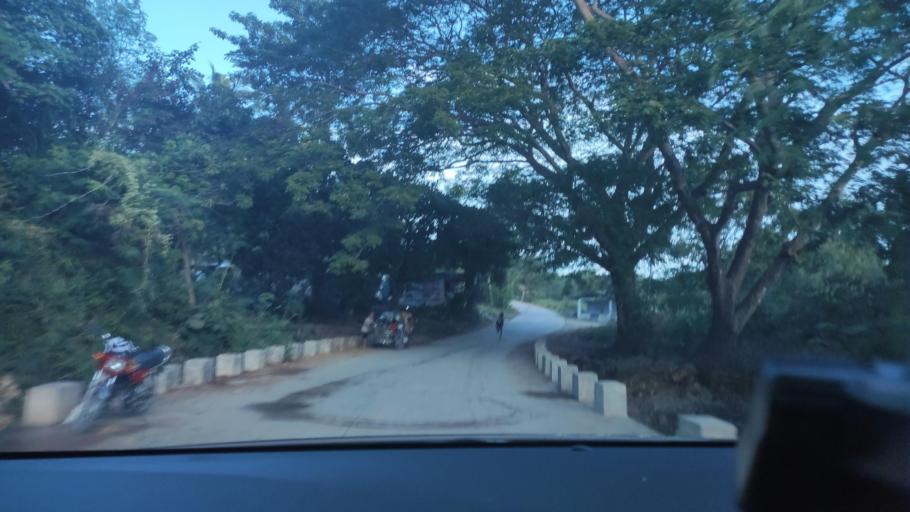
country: PH
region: Ilocos
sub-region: Province of Pangasinan
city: Balingasay
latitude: 16.3051
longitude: 119.8600
